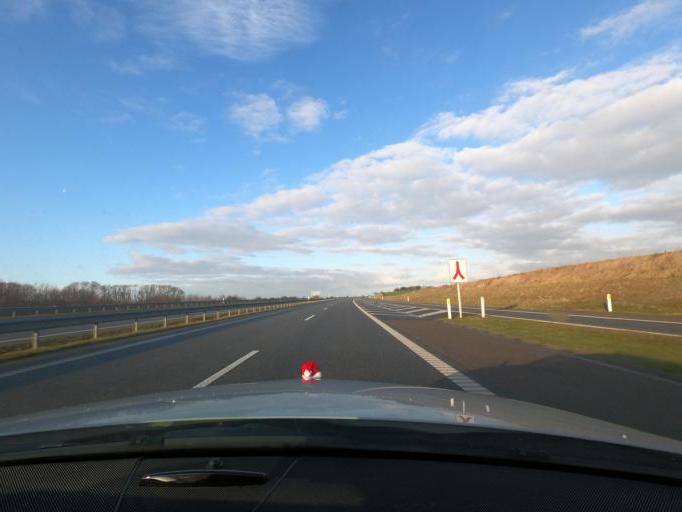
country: DK
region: South Denmark
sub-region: Sonderborg Kommune
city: Dybbol
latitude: 54.9252
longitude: 9.7213
